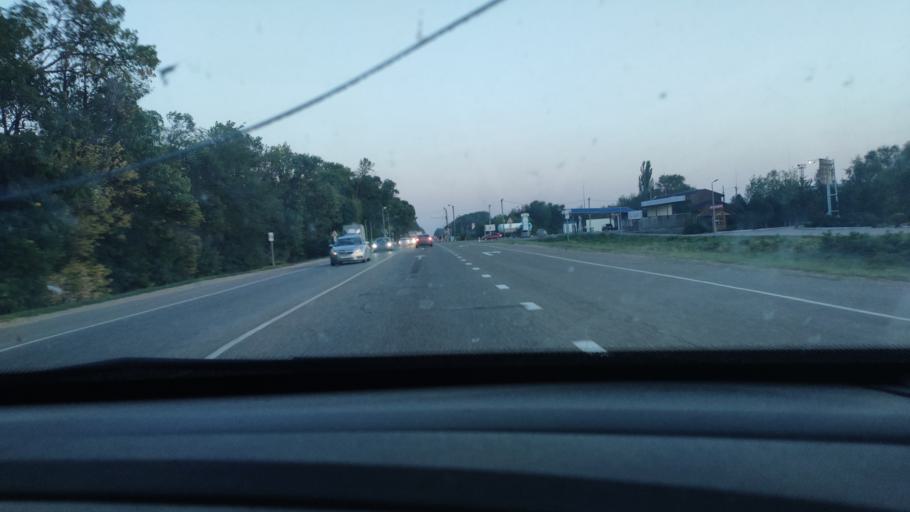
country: RU
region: Krasnodarskiy
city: Medvedovskaya
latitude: 45.4498
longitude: 38.9918
